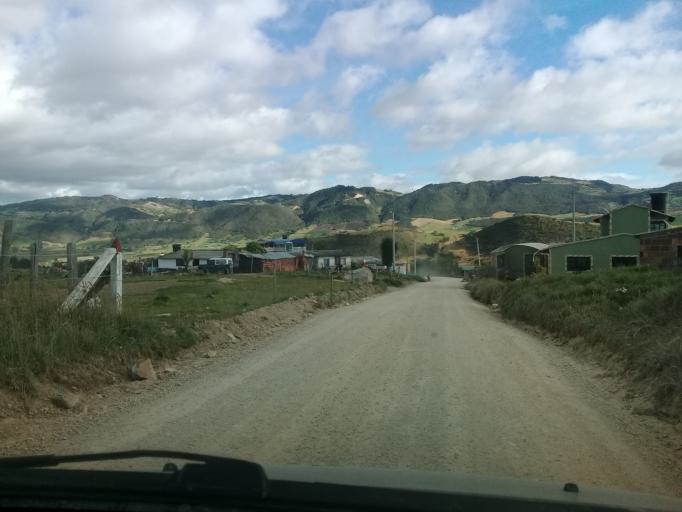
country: CO
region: Cundinamarca
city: Lenguazaque
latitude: 5.2807
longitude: -73.6694
